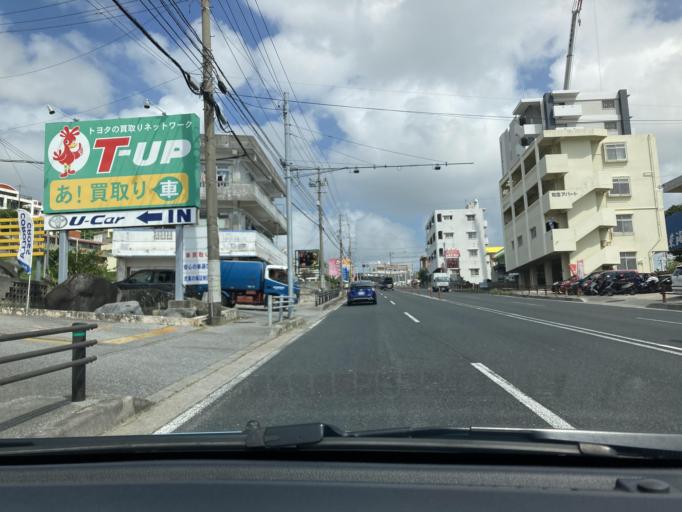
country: JP
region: Okinawa
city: Okinawa
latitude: 26.3291
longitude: 127.8222
